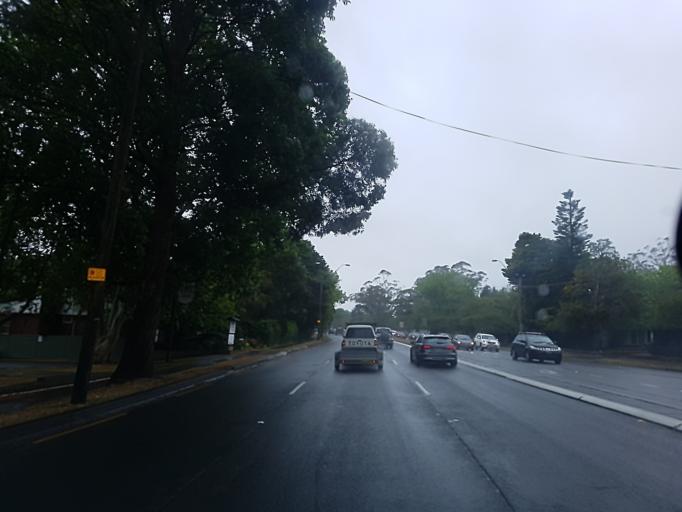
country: AU
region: New South Wales
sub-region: City of Sydney
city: North Turramurra
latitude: -33.7269
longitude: 151.1661
